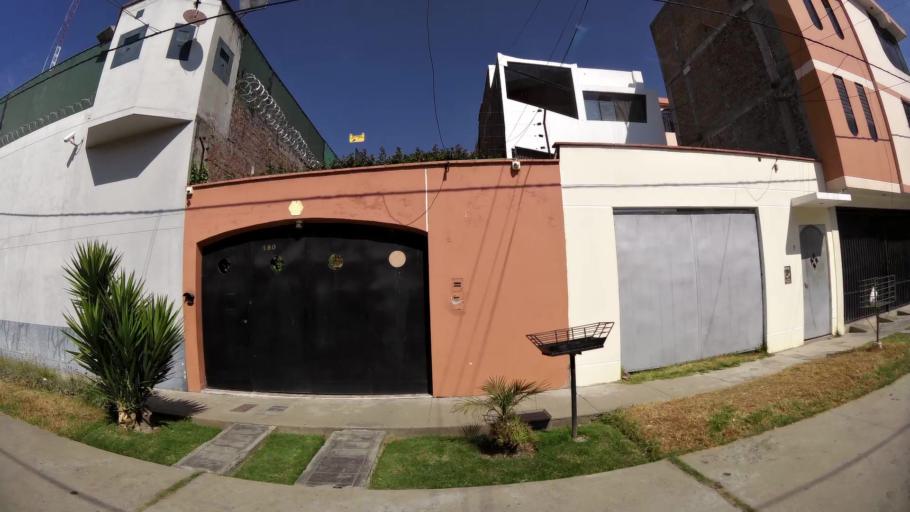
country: PE
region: Junin
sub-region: Provincia de Huancayo
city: El Tambo
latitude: -12.0792
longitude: -75.2290
